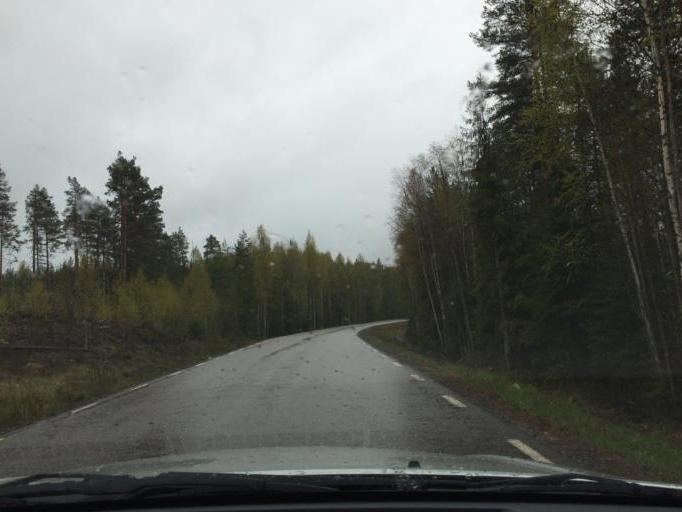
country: SE
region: Dalarna
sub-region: Ludvika Kommun
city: Grangesberg
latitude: 60.0397
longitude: 14.9095
